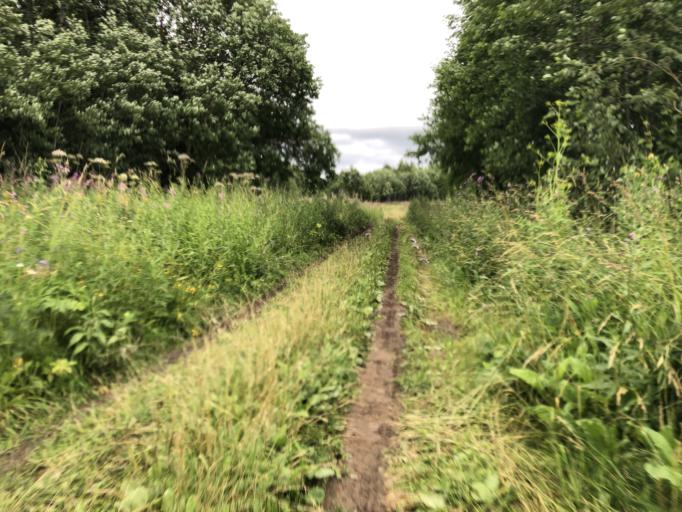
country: RU
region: Tverskaya
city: Rzhev
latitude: 56.2386
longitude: 34.3824
